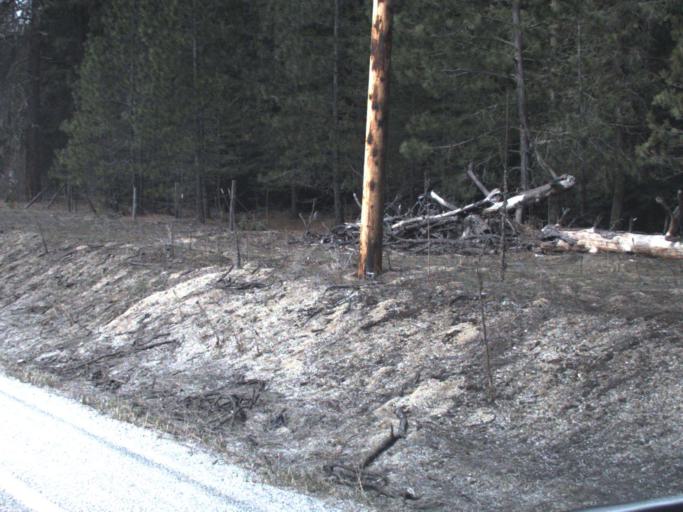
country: US
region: Washington
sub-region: Pend Oreille County
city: Newport
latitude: 48.4695
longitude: -117.3179
